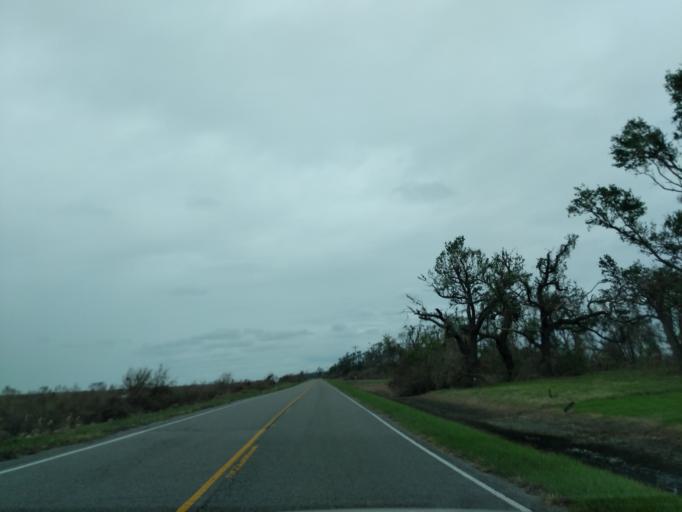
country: US
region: Louisiana
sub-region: Cameron Parish
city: Cameron
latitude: 29.7860
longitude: -93.1179
